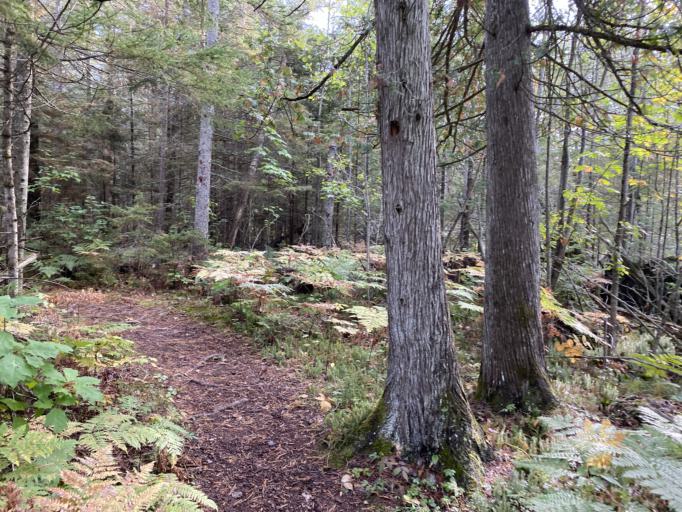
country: US
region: Michigan
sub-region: Mackinac County
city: Saint Ignace
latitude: 45.7425
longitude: -84.8919
